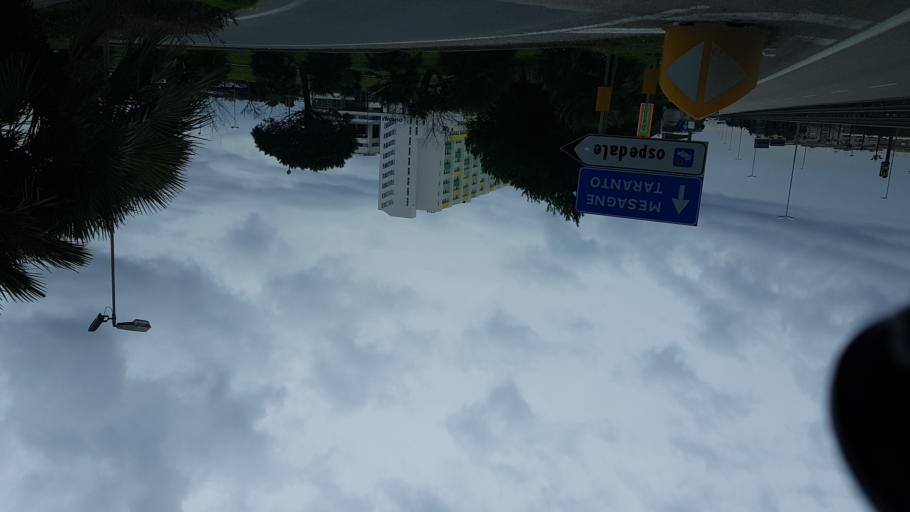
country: IT
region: Apulia
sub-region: Provincia di Brindisi
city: Brindisi
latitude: 40.6254
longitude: 17.9182
